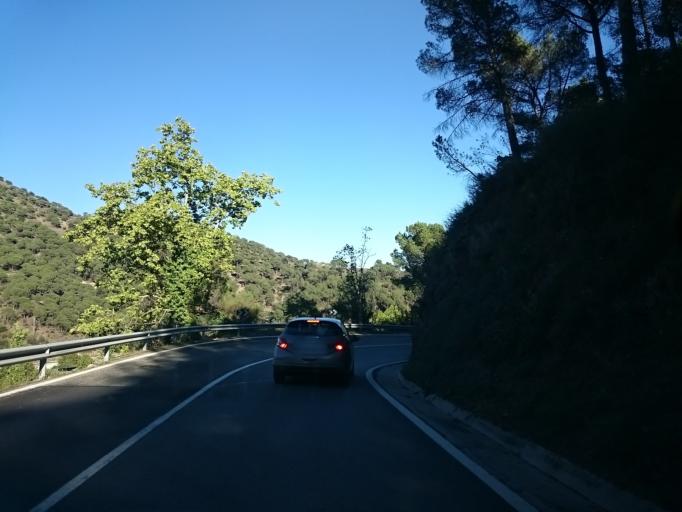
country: ES
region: Catalonia
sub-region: Provincia de Barcelona
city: Capellades
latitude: 41.5245
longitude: 1.6889
